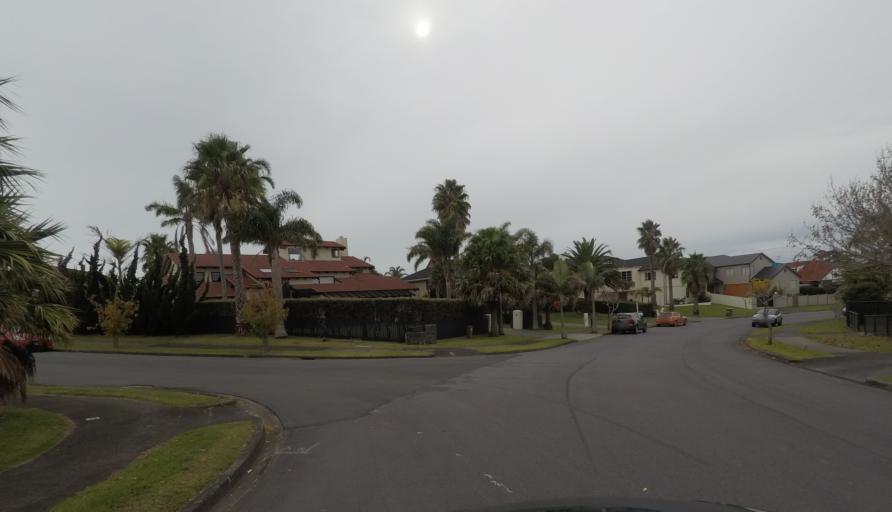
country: NZ
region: Auckland
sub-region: Auckland
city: Pakuranga
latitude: -36.8955
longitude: 174.9484
